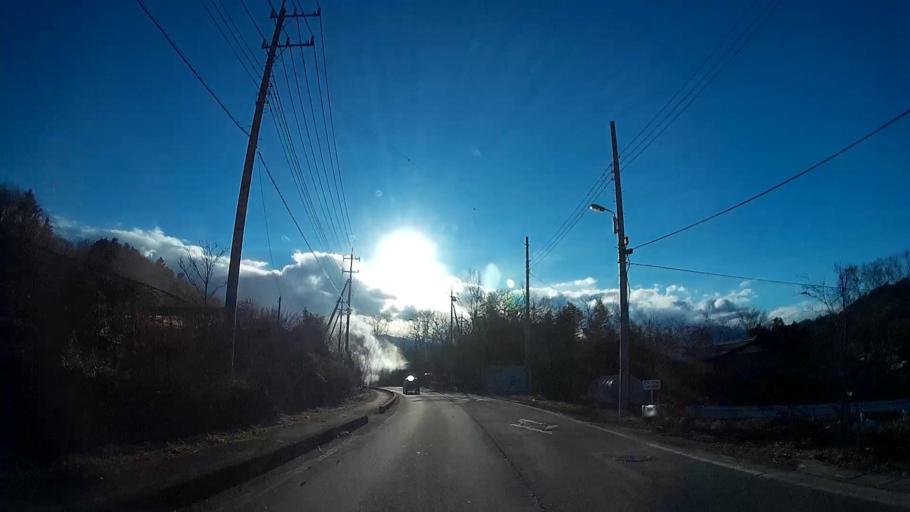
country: JP
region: Saitama
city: Chichibu
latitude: 36.0479
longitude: 139.0507
